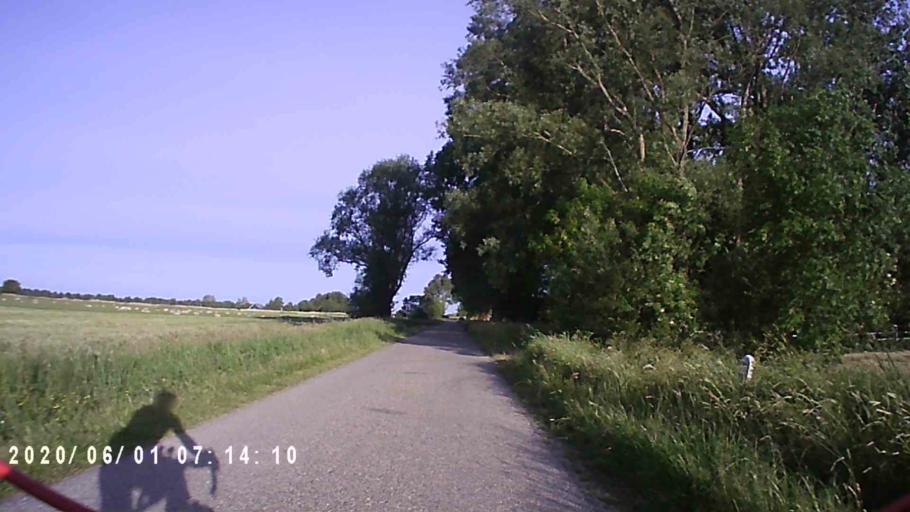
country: NL
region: Friesland
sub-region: Gemeente Dantumadiel
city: Walterswald
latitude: 53.3136
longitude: 6.0533
